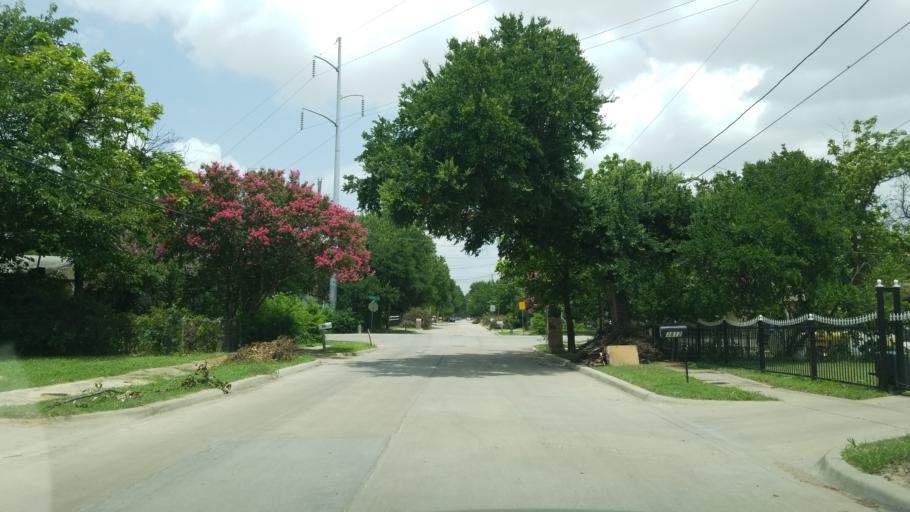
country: US
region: Texas
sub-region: Dallas County
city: Cockrell Hill
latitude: 32.7885
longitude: -96.8970
